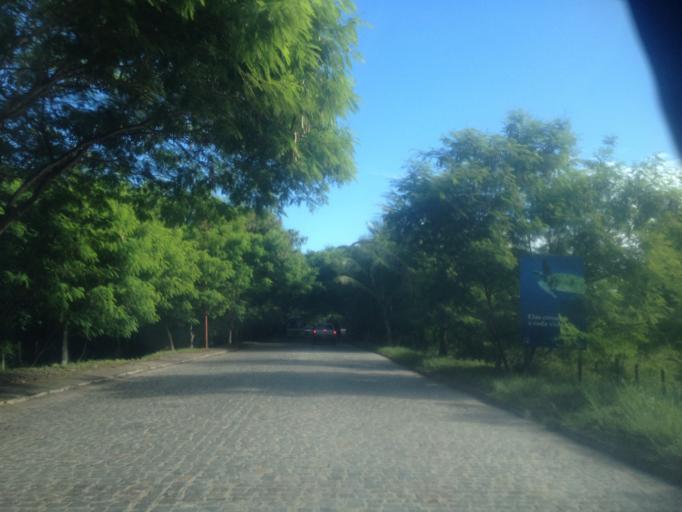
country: BR
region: Bahia
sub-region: Mata De Sao Joao
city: Mata de Sao Joao
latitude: -12.5737
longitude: -38.0146
